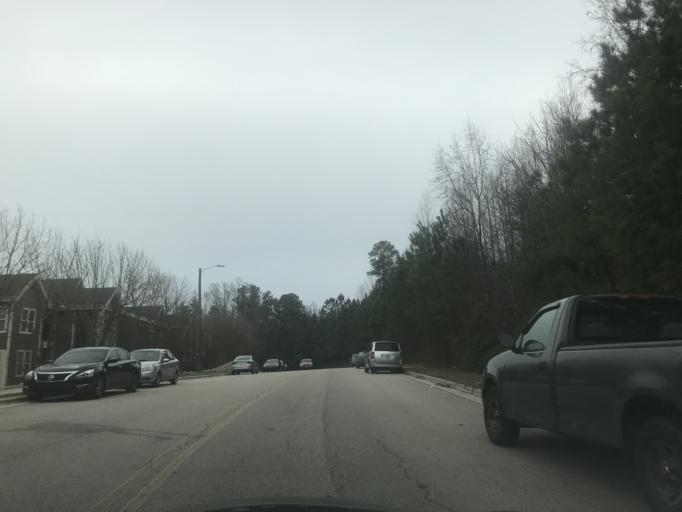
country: US
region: North Carolina
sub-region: Wake County
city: Raleigh
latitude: 35.8751
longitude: -78.5868
